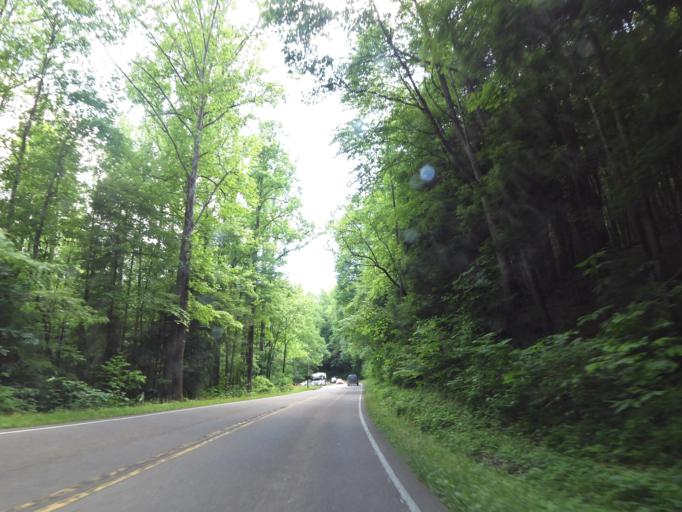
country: US
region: Tennessee
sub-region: Sevier County
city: Gatlinburg
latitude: 35.6736
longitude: -83.5263
